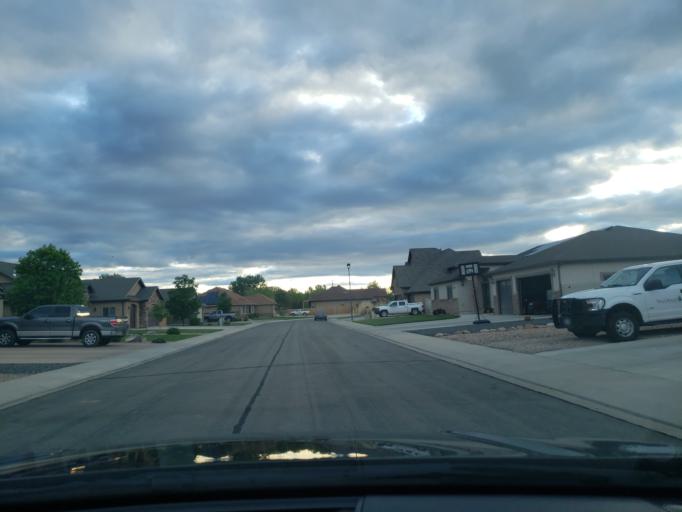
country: US
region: Colorado
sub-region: Mesa County
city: Fruita
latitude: 39.1658
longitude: -108.7084
